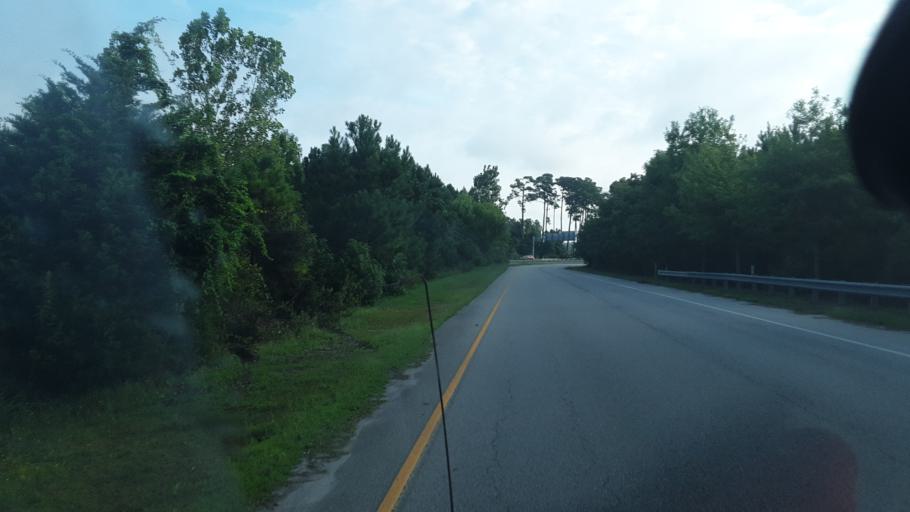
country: US
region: South Carolina
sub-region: Horry County
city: Myrtle Beach
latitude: 33.7386
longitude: -78.8481
